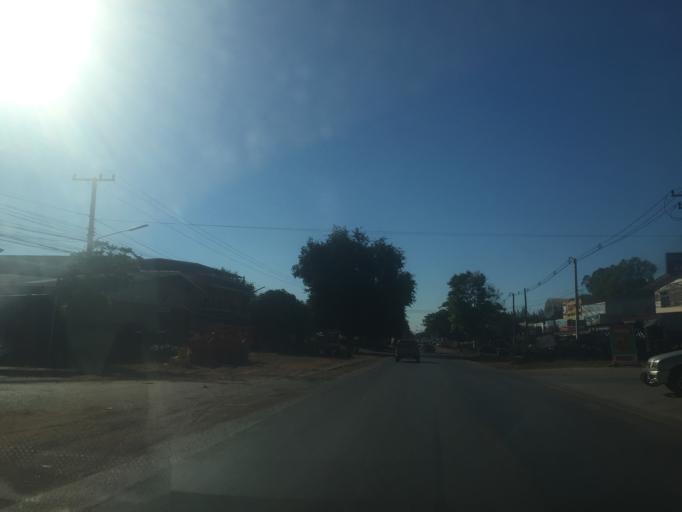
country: TH
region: Changwat Udon Thani
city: Si That
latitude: 16.9741
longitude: 103.2247
